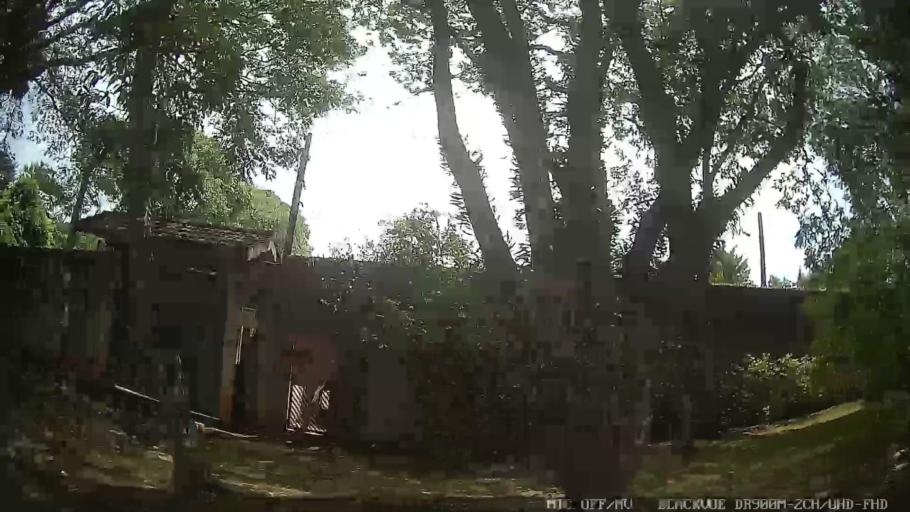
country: BR
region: Sao Paulo
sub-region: Atibaia
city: Atibaia
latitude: -23.1185
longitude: -46.5969
